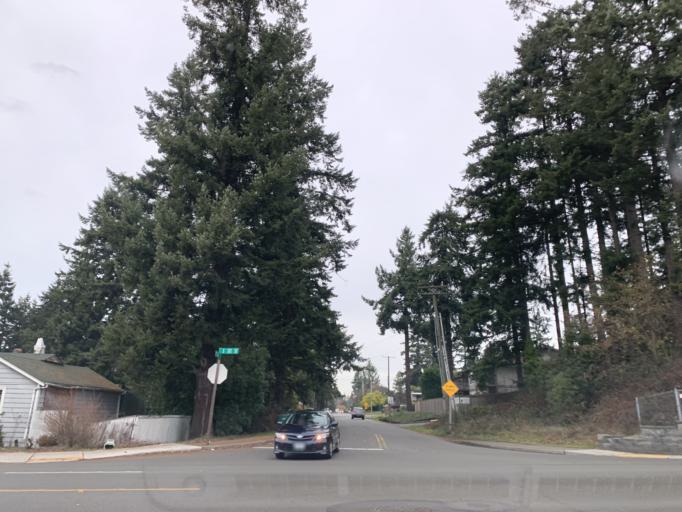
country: US
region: Washington
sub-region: King County
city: Federal Way
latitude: 47.3223
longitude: -122.3108
